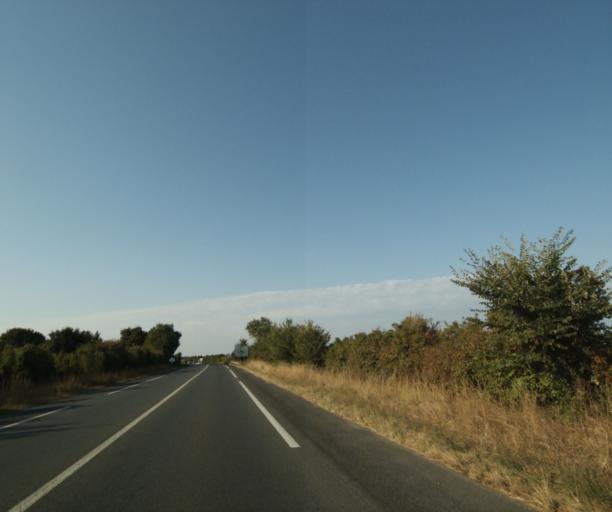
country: FR
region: Poitou-Charentes
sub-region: Departement de la Charente-Maritime
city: Saint-Hippolyte
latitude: 45.9203
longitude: -0.8850
